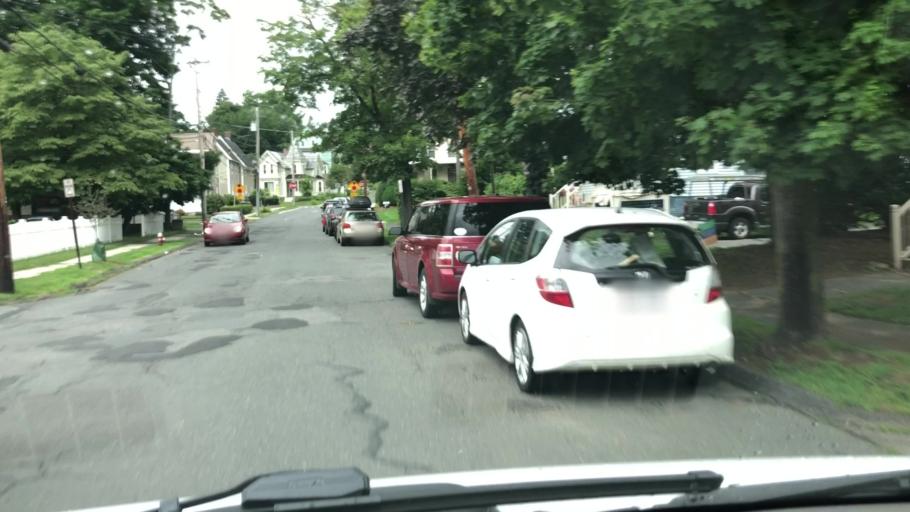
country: US
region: Massachusetts
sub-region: Hampshire County
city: Northampton
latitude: 42.3220
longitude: -72.6330
